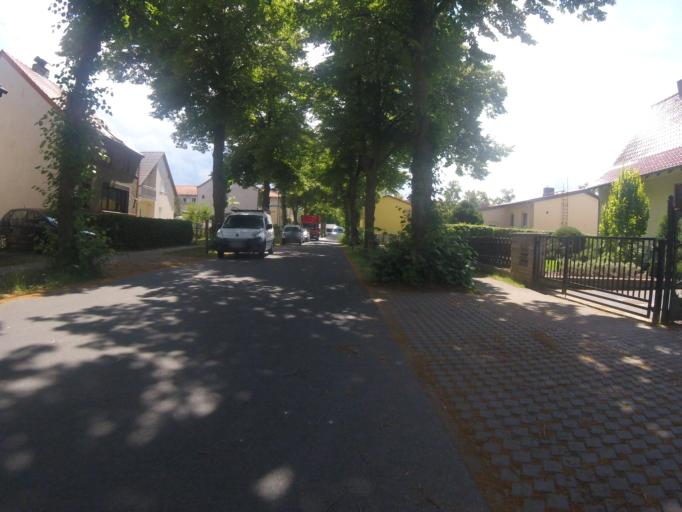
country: DE
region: Brandenburg
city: Konigs Wusterhausen
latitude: 52.2759
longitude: 13.6412
